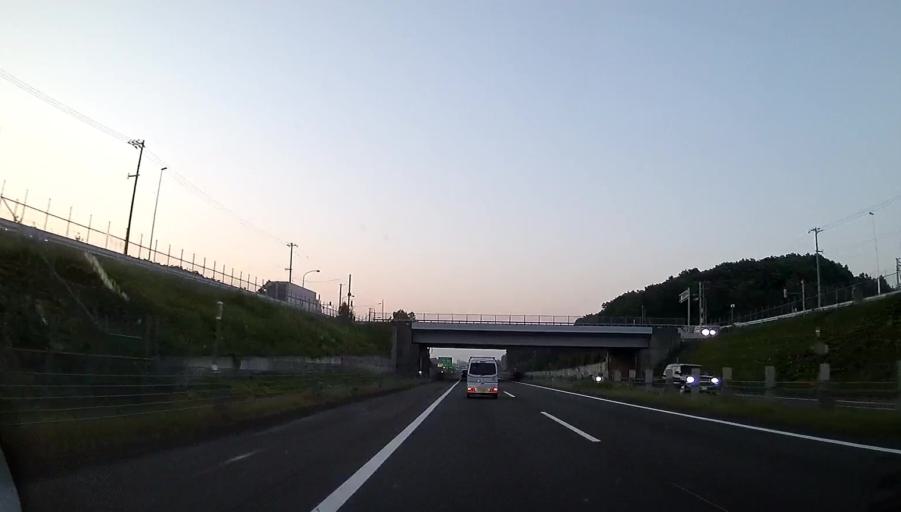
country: JP
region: Hokkaido
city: Kitahiroshima
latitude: 43.0009
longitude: 141.4677
